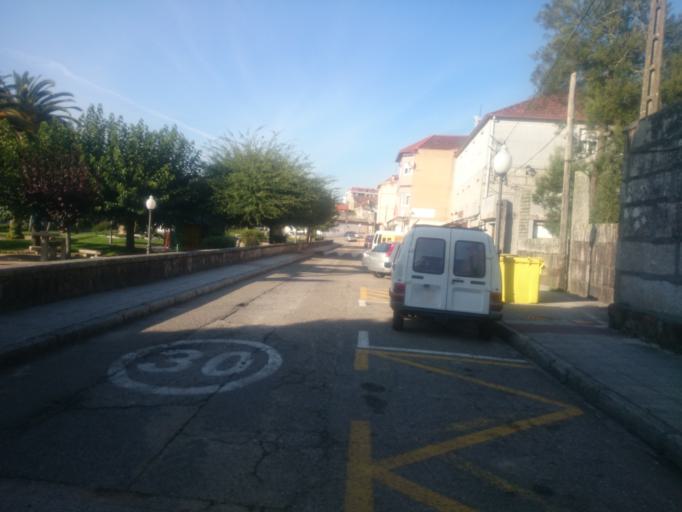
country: ES
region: Galicia
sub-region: Provincia de Pontevedra
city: Porrino
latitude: 42.1570
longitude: -8.6191
